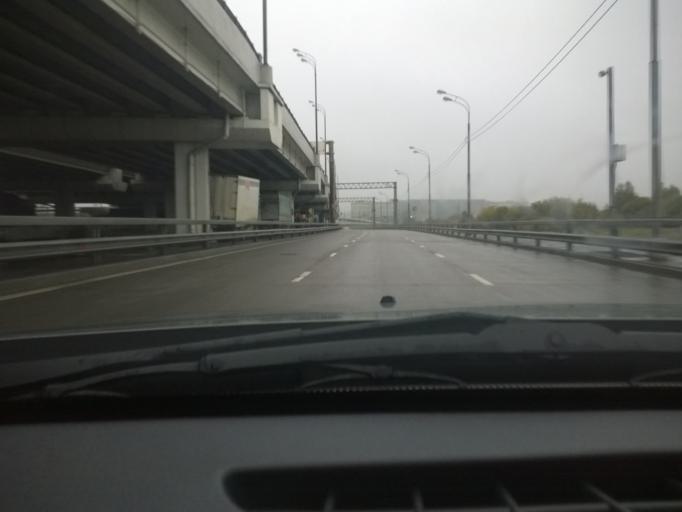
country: RU
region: Moscow
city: Zhulebino
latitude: 55.7104
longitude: 37.8475
